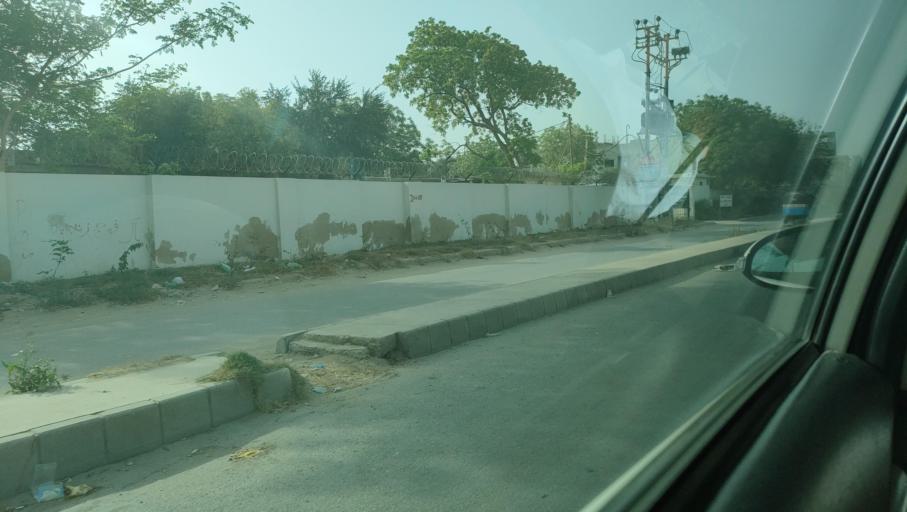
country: PK
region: Sindh
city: Malir Cantonment
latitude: 24.9071
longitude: 67.1832
